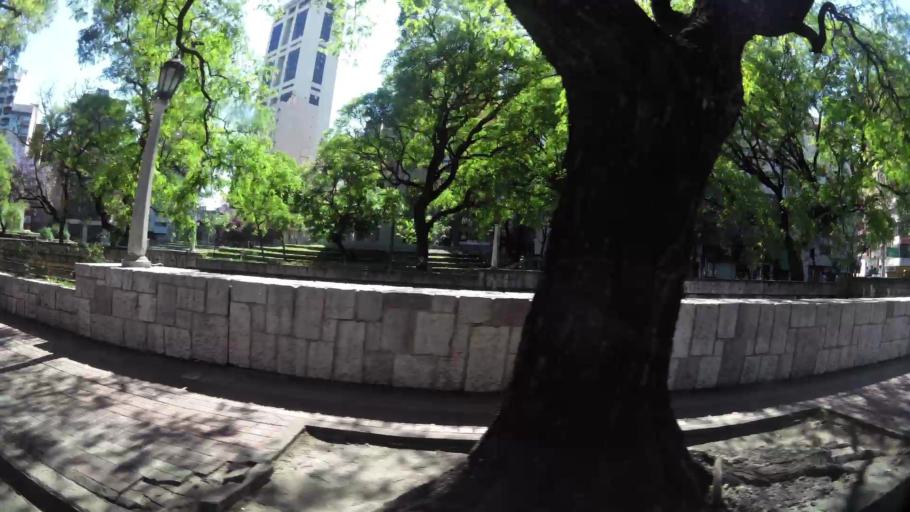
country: AR
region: Cordoba
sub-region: Departamento de Capital
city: Cordoba
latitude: -31.4164
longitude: -64.1907
